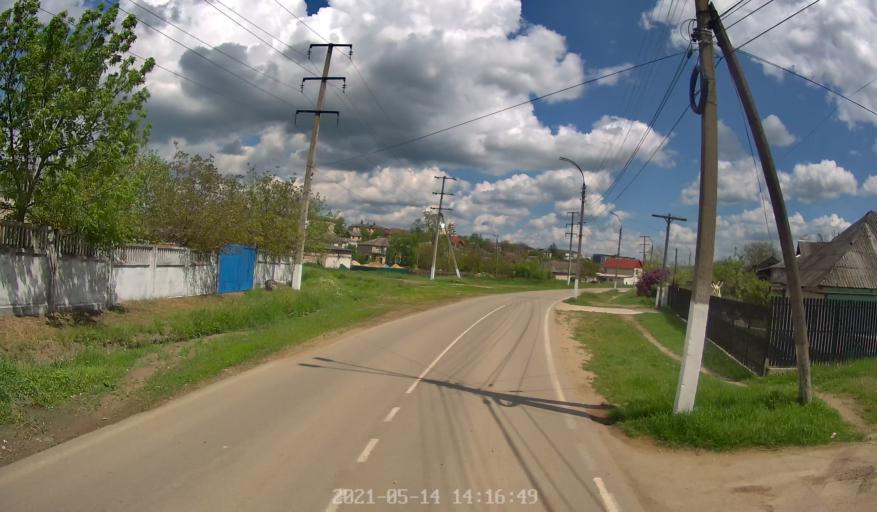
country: MD
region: Hincesti
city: Hincesti
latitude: 46.8244
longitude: 28.5888
